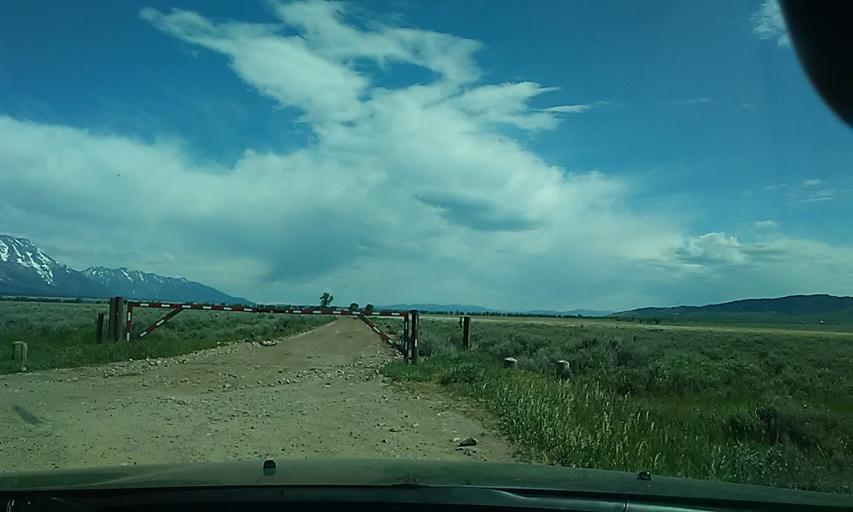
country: US
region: Wyoming
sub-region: Teton County
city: Jackson
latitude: 43.6308
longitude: -110.6640
